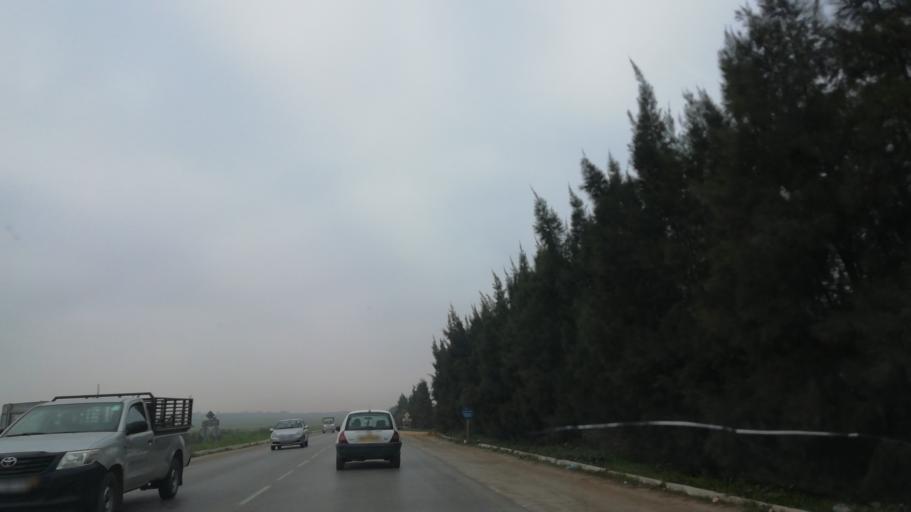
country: DZ
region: Relizane
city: Djidiouia
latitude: 35.9031
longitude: 0.7694
